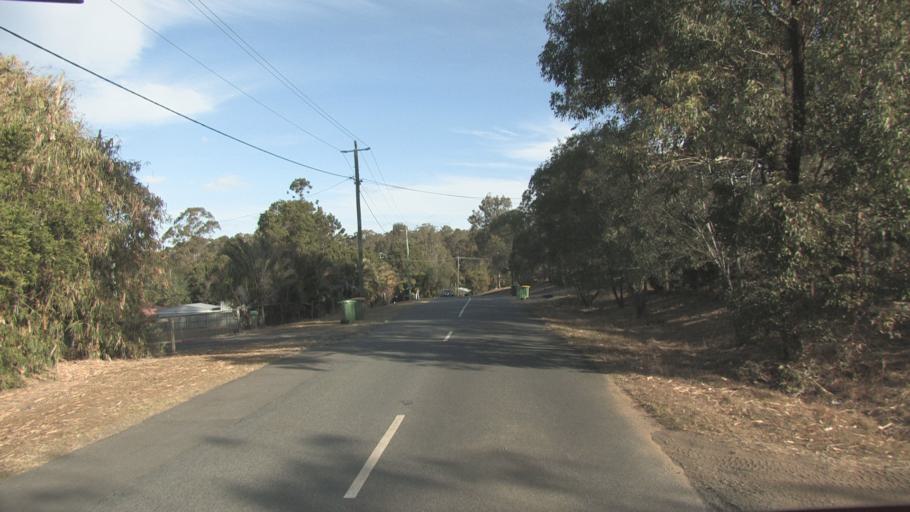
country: AU
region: Queensland
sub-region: Logan
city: Cedar Vale
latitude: -27.8781
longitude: 153.0104
